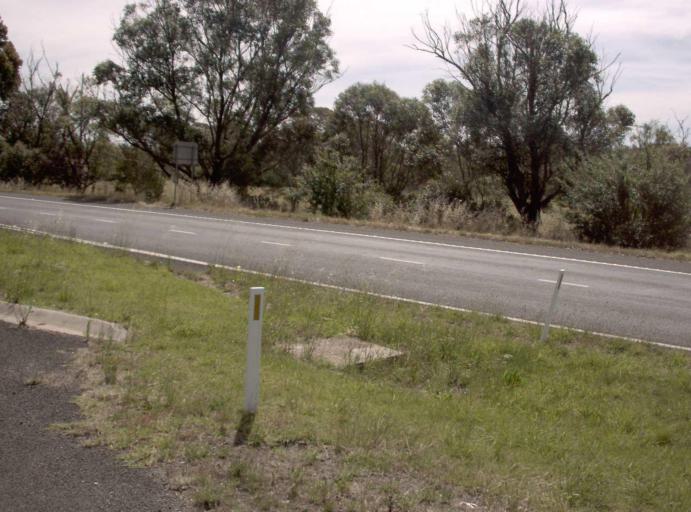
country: AU
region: Victoria
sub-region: Wellington
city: Heyfield
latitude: -38.1526
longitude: 146.7684
